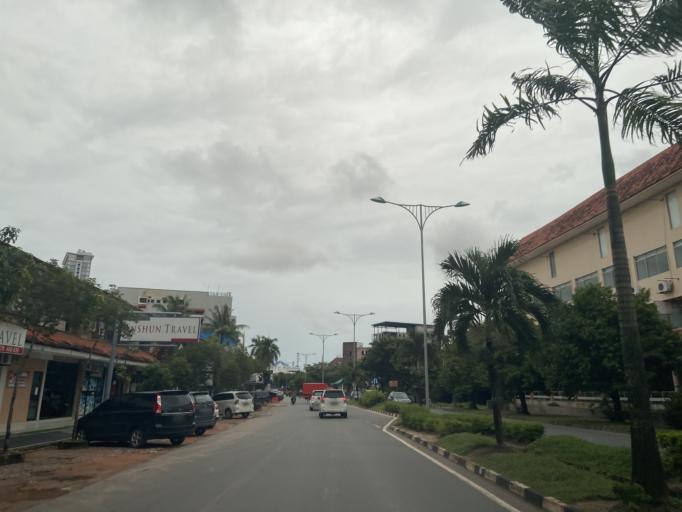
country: SG
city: Singapore
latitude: 1.1312
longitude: 104.0501
